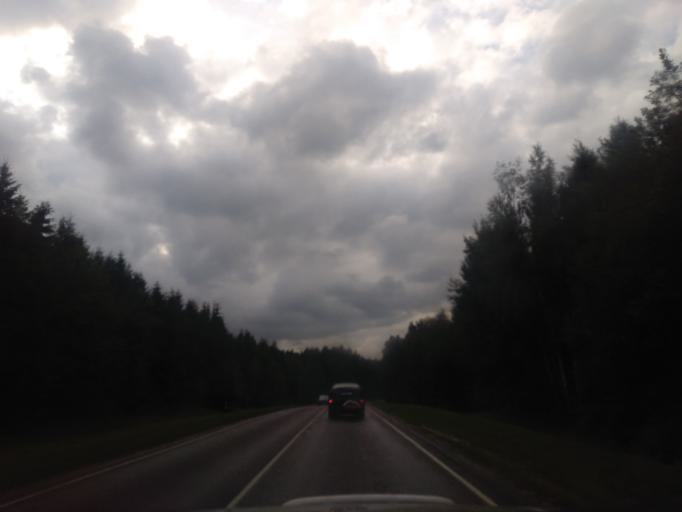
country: BY
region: Minsk
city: Enyerhyetykaw
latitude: 53.5430
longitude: 27.0581
